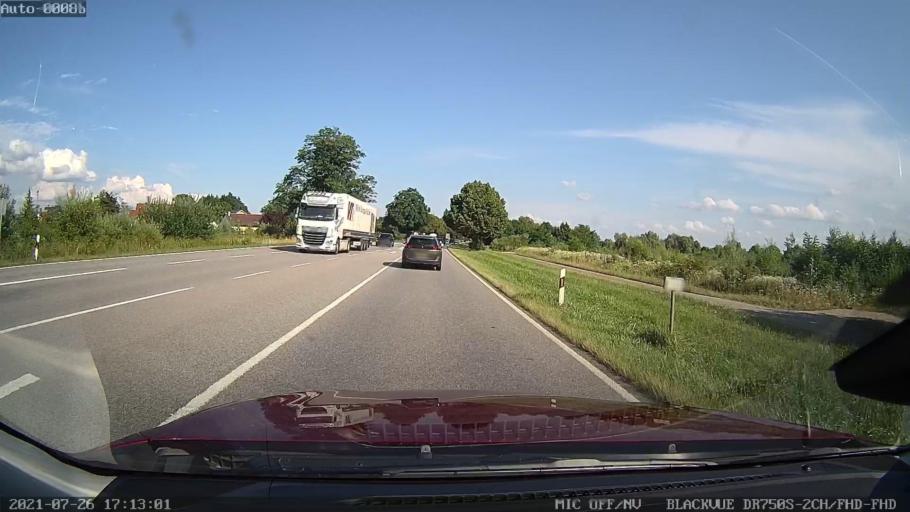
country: DE
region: Bavaria
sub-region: Upper Palatinate
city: Riekofen
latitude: 48.9727
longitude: 12.3120
